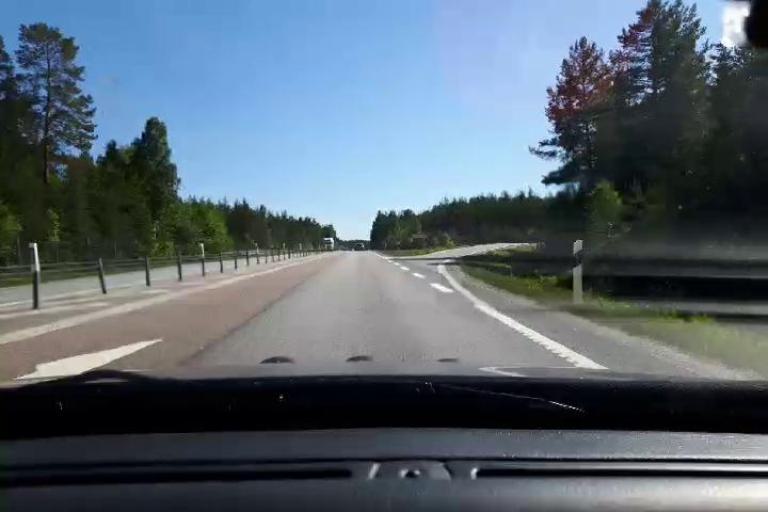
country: SE
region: Gaevleborg
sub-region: Soderhamns Kommun
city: Ljusne
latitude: 61.1249
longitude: 17.0148
